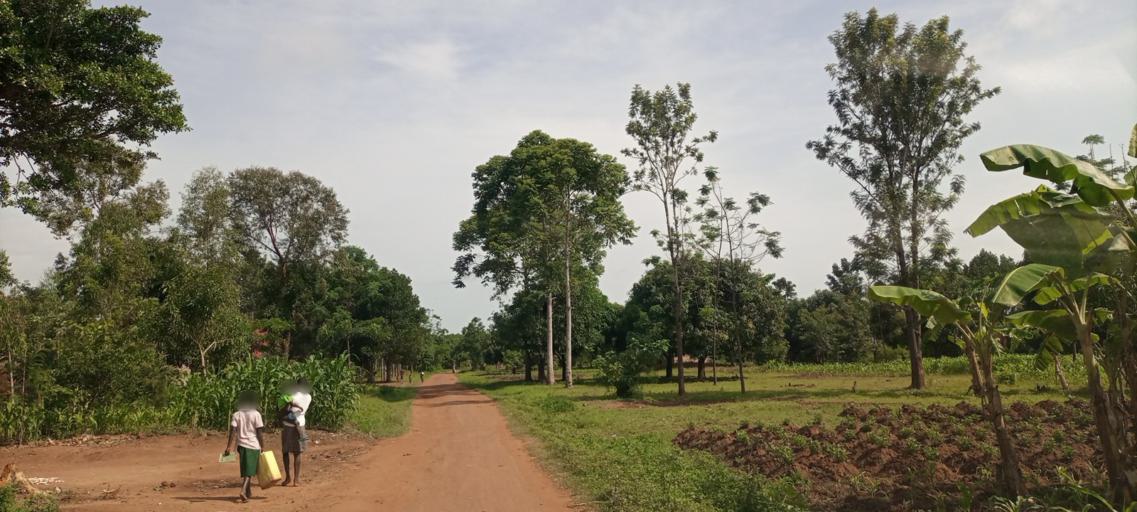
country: UG
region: Eastern Region
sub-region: Mbale District
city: Mbale
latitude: 1.1273
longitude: 34.0269
